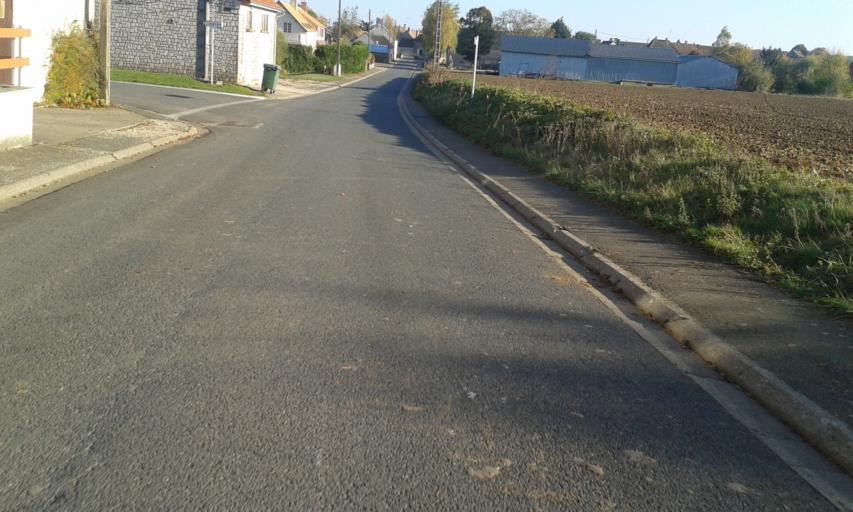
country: FR
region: Centre
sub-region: Departement du Loir-et-Cher
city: Ouzouer-le-Marche
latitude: 47.8808
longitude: 1.4174
